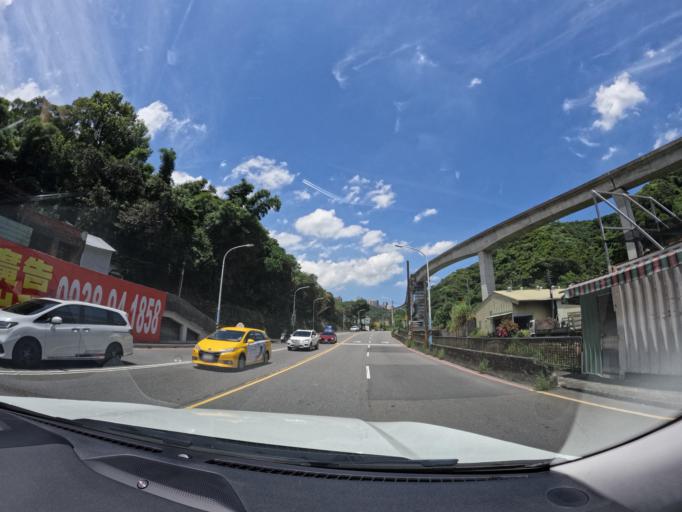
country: TW
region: Taipei
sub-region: Taipei
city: Banqiao
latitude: 25.0280
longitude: 121.4070
